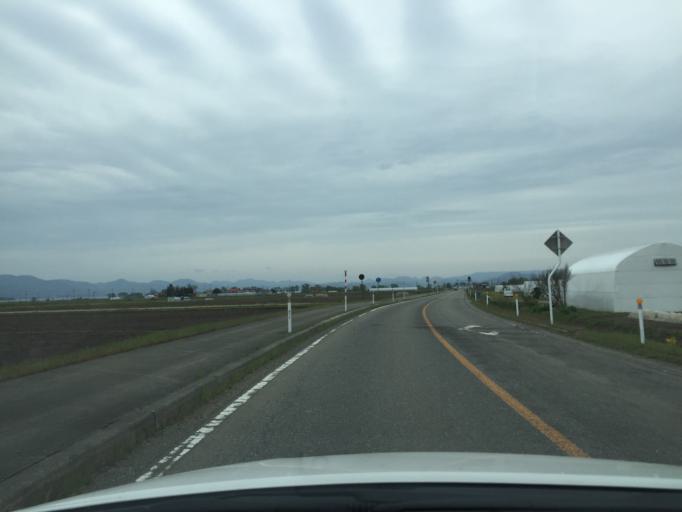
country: JP
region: Fukushima
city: Inawashiro
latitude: 37.5435
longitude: 140.0778
